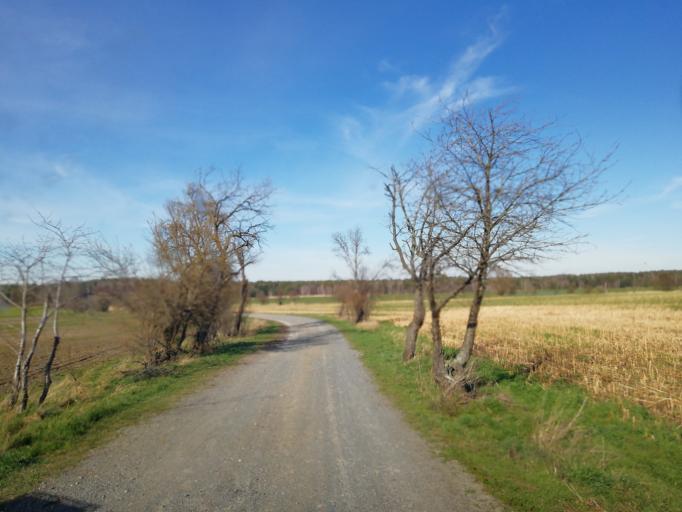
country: DE
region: Brandenburg
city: Ruckersdorf
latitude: 51.5567
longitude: 13.5926
